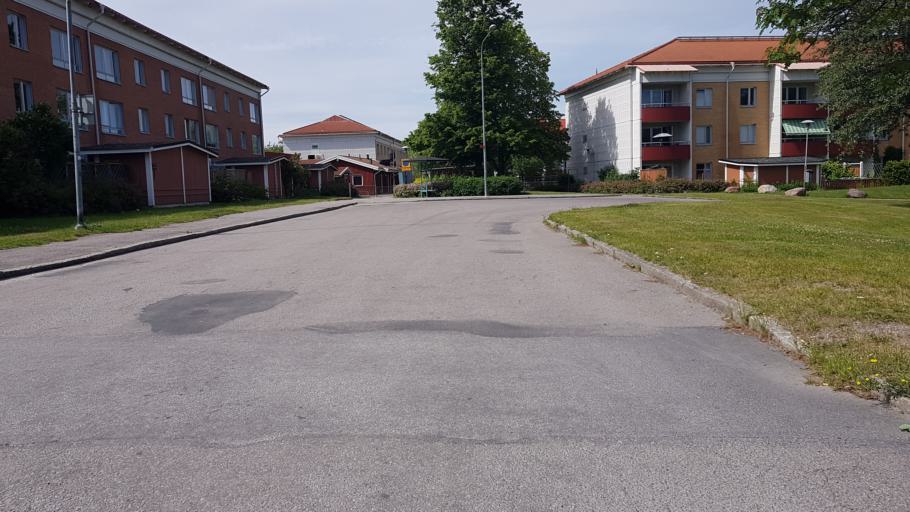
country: SE
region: OEstergoetland
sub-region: Norrkopings Kommun
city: Norrkoping
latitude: 58.5754
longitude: 16.2093
